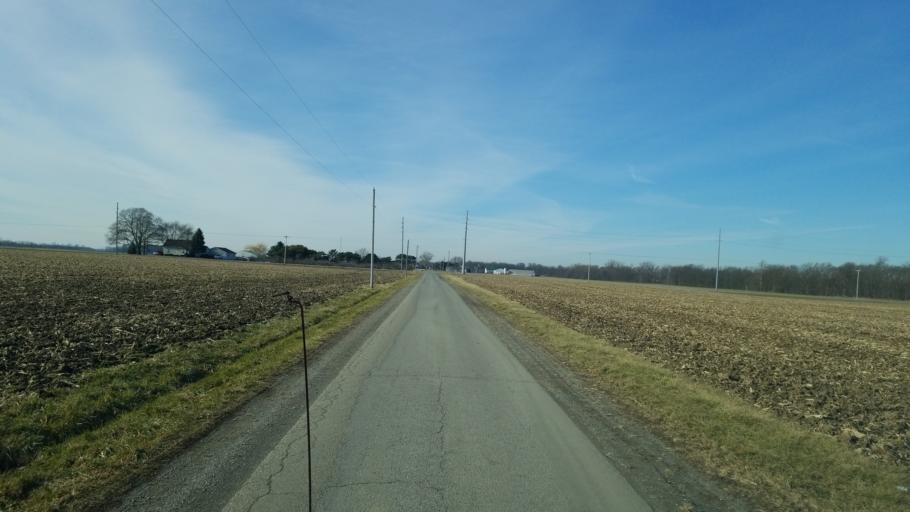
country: US
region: Ohio
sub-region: Putnam County
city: Pandora
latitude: 41.0071
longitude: -83.9537
